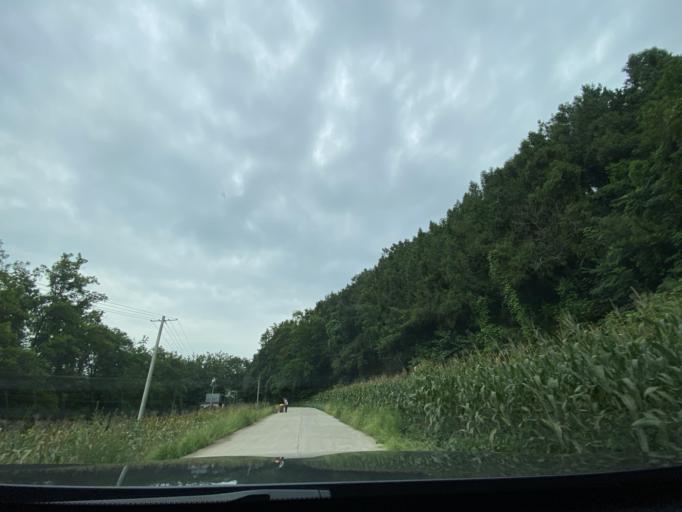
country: CN
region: Sichuan
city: Jiancheng
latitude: 30.3882
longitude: 104.5101
